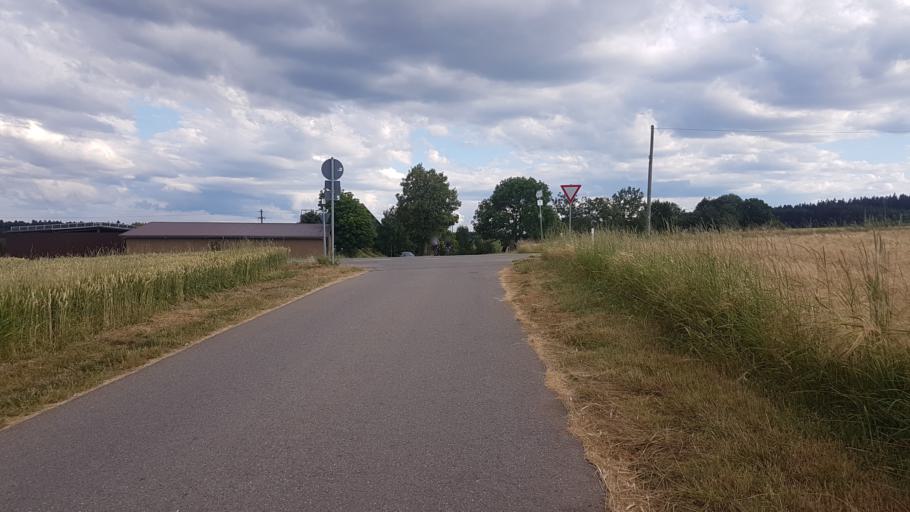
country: DE
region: Baden-Wuerttemberg
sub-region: Freiburg Region
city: Unterkirnach
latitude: 48.0309
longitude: 8.4085
